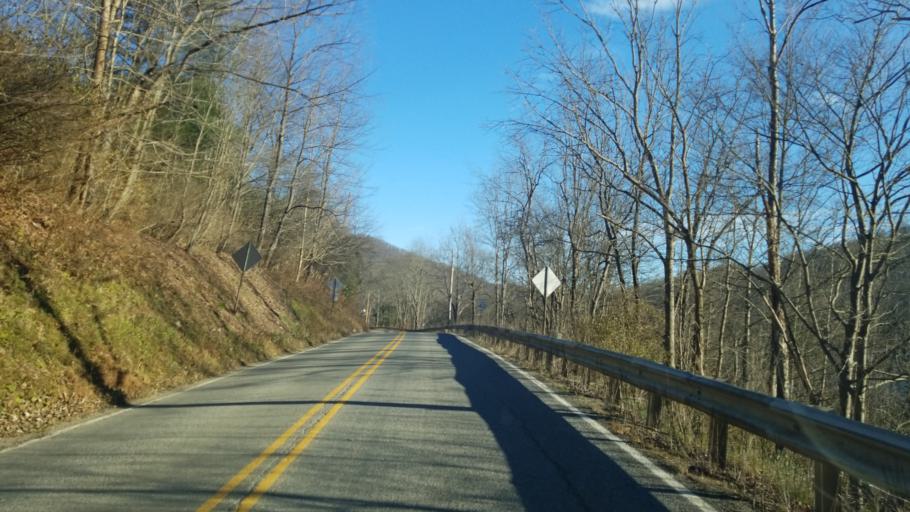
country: US
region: Pennsylvania
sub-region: Potter County
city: Coudersport
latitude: 41.6329
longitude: -78.1001
